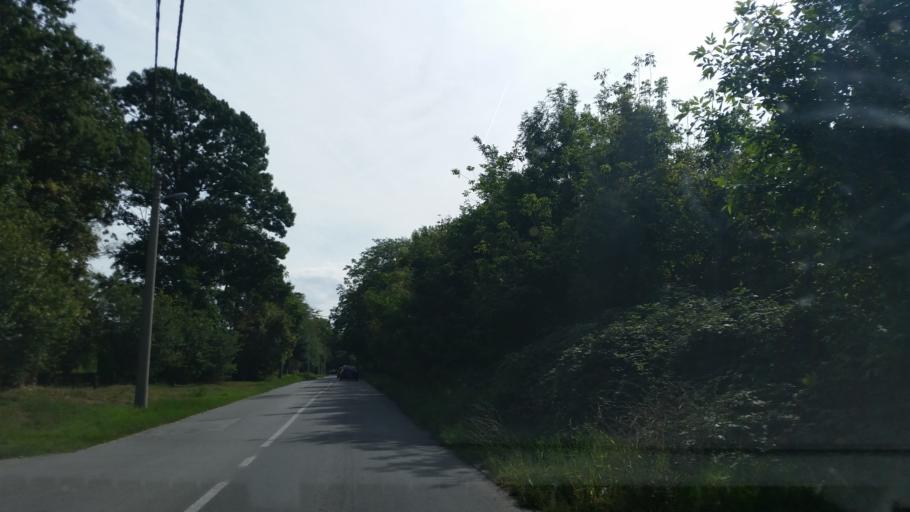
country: RS
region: Central Serbia
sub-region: Belgrade
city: Palilula
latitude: 44.8091
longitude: 20.5016
